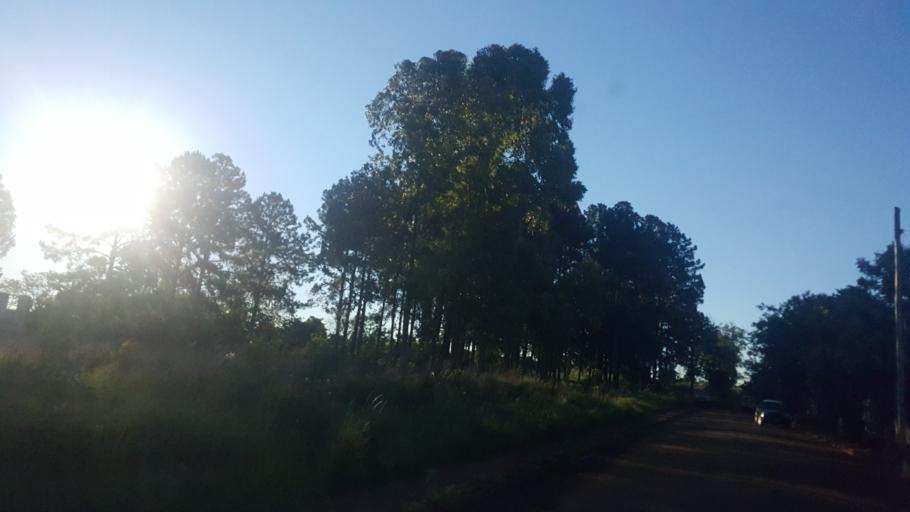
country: AR
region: Misiones
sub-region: Departamento de Capital
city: Posadas
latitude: -27.4278
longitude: -55.9438
